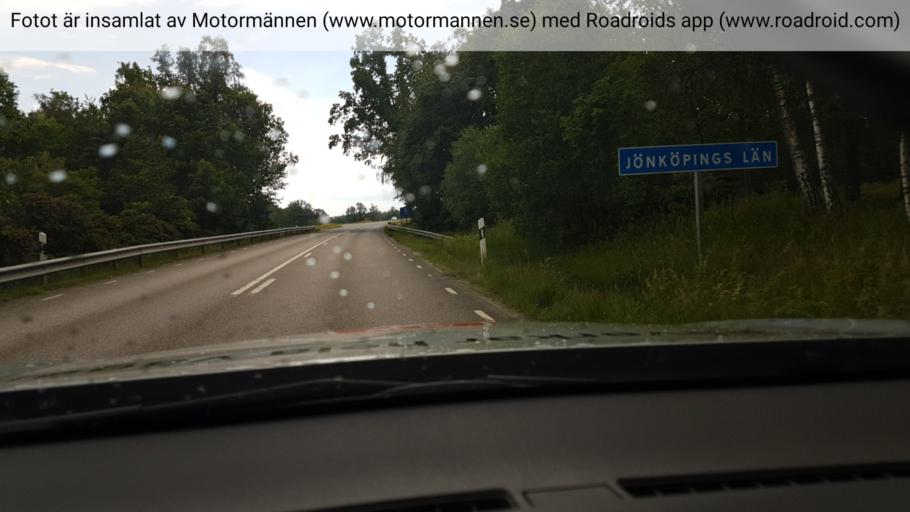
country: SE
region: Vaestra Goetaland
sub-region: Hjo Kommun
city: Hjo
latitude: 58.1362
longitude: 14.2191
